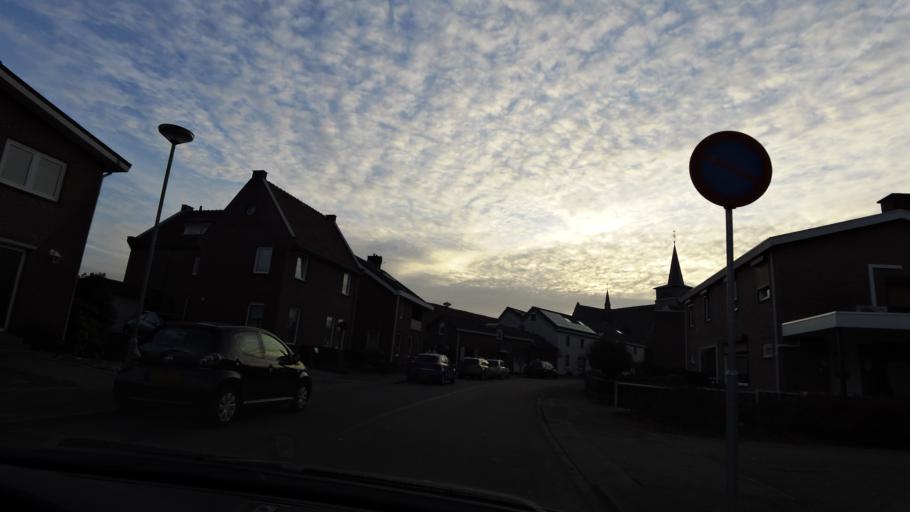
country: NL
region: Limburg
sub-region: Gemeente Schinnen
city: Puth
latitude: 50.9389
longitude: 5.8391
